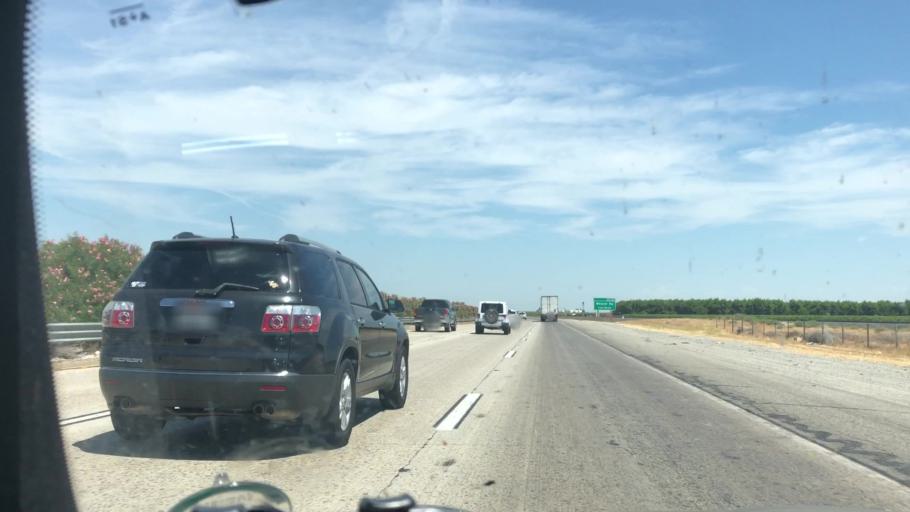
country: US
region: California
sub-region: Kern County
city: McFarland
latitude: 35.6117
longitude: -119.2118
